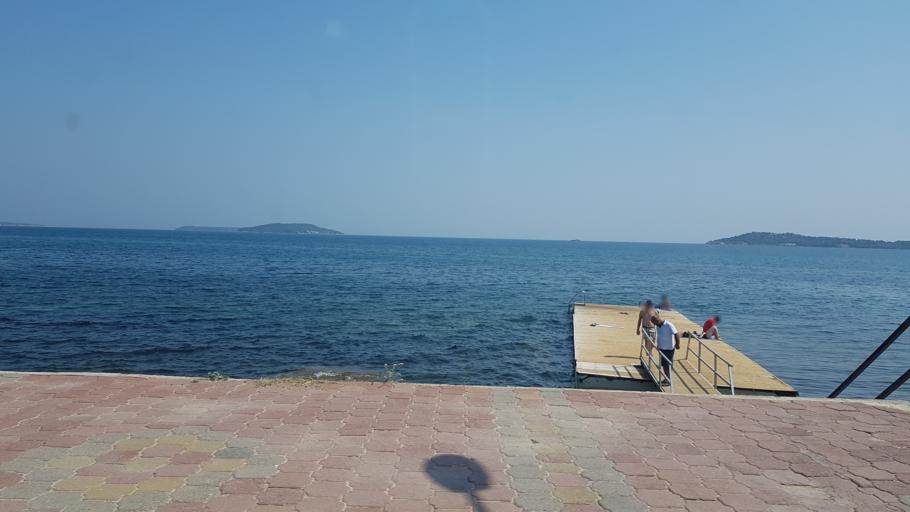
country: TR
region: Izmir
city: Urla
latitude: 38.3705
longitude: 26.7632
